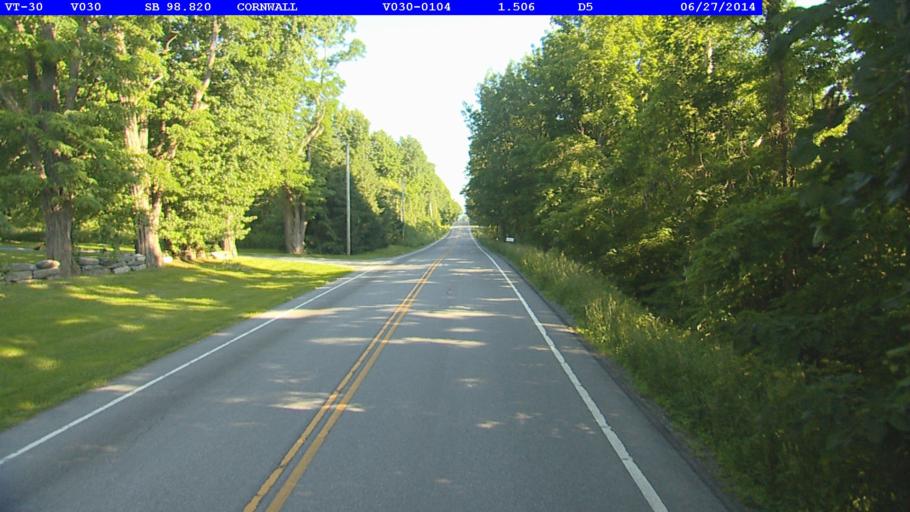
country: US
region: Vermont
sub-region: Addison County
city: Middlebury (village)
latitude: 43.9294
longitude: -73.2126
